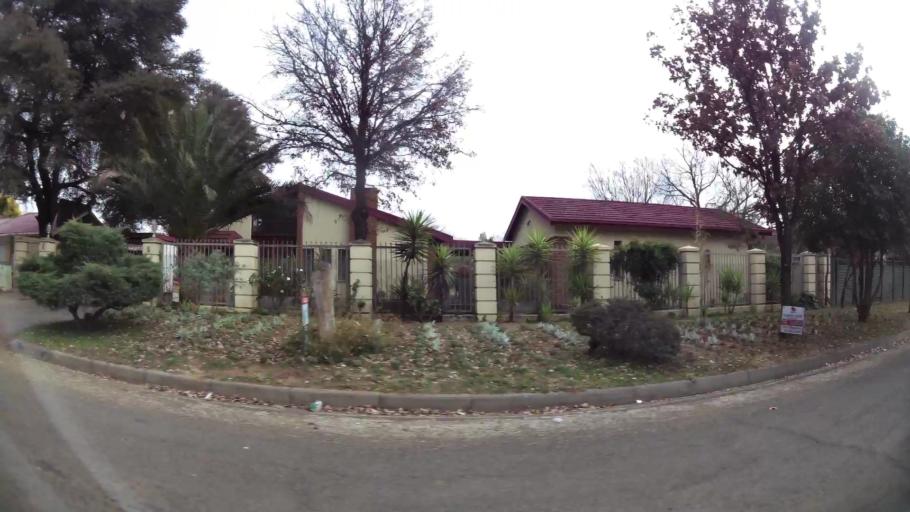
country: ZA
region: Orange Free State
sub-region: Mangaung Metropolitan Municipality
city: Bloemfontein
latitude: -29.1234
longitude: 26.1906
